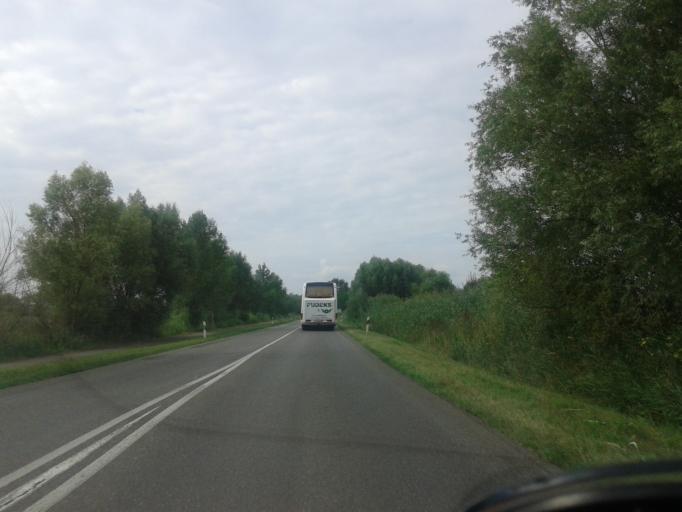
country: HU
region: Bacs-Kiskun
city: Soltvadkert
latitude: 46.5658
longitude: 19.4092
